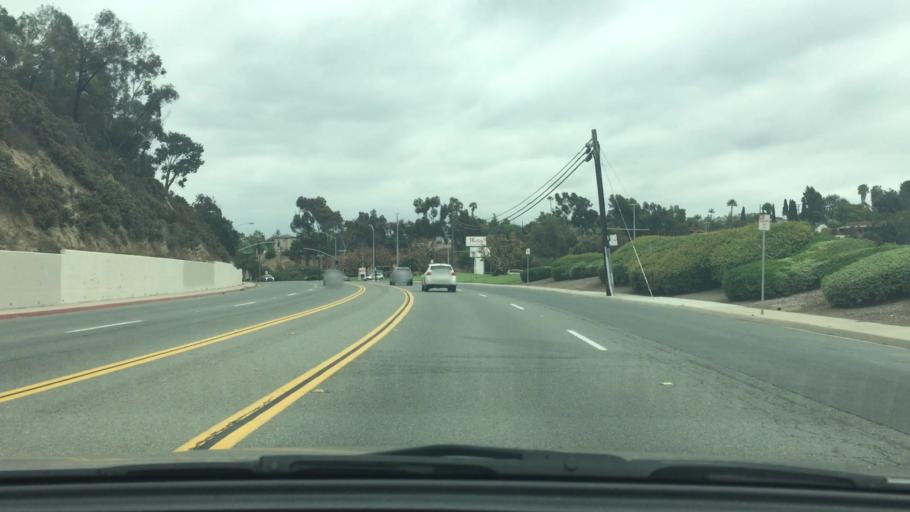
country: US
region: California
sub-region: San Diego County
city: Chula Vista
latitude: 32.6592
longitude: -117.0652
